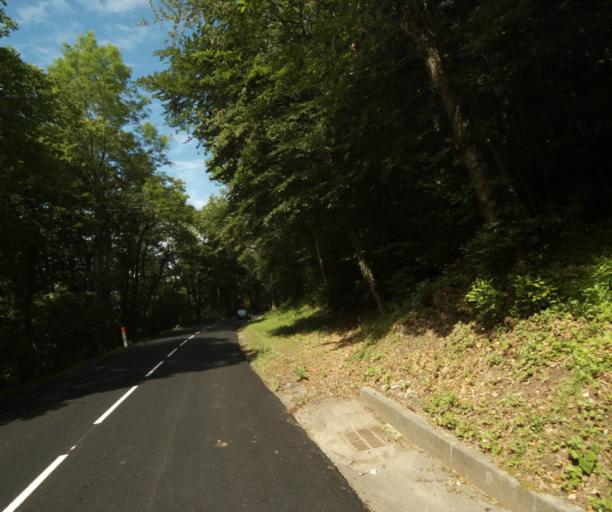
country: FR
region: Rhone-Alpes
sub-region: Departement de la Haute-Savoie
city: Perrignier
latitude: 46.3033
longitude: 6.4633
